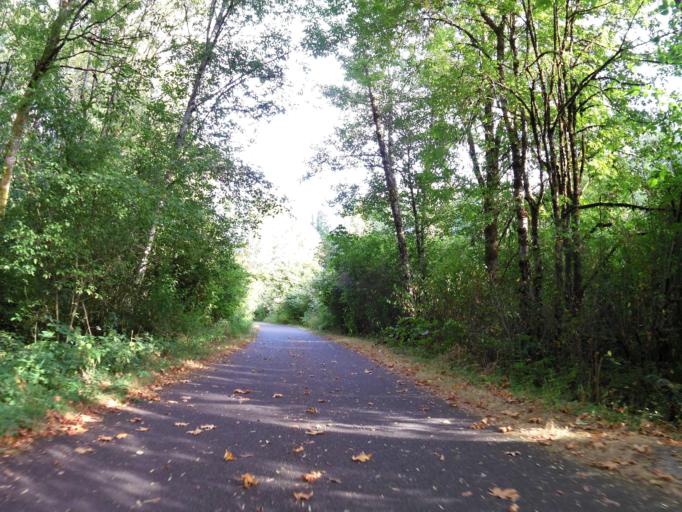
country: US
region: Washington
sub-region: Thurston County
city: Lacey
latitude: 46.9802
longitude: -122.8226
